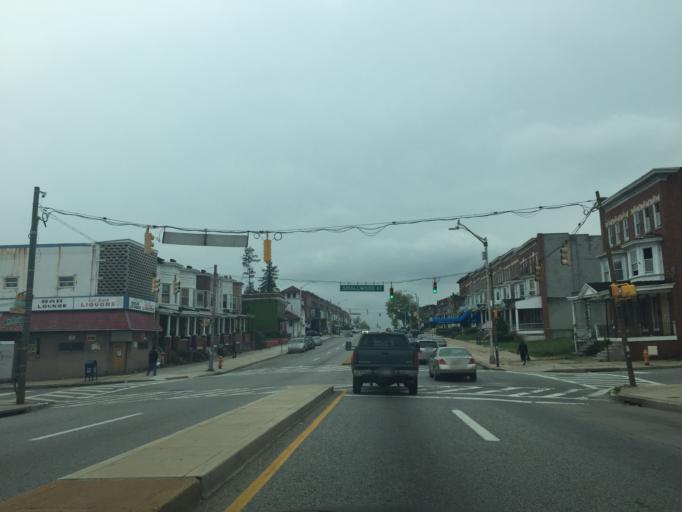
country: US
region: Maryland
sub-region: City of Baltimore
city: Baltimore
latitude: 39.3097
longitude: -76.6523
